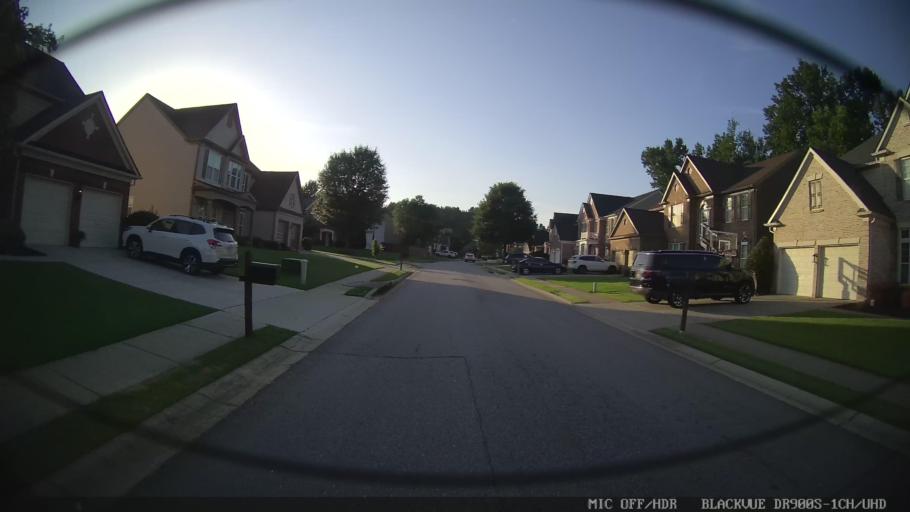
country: US
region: Georgia
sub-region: Forsyth County
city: Cumming
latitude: 34.2162
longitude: -84.2319
